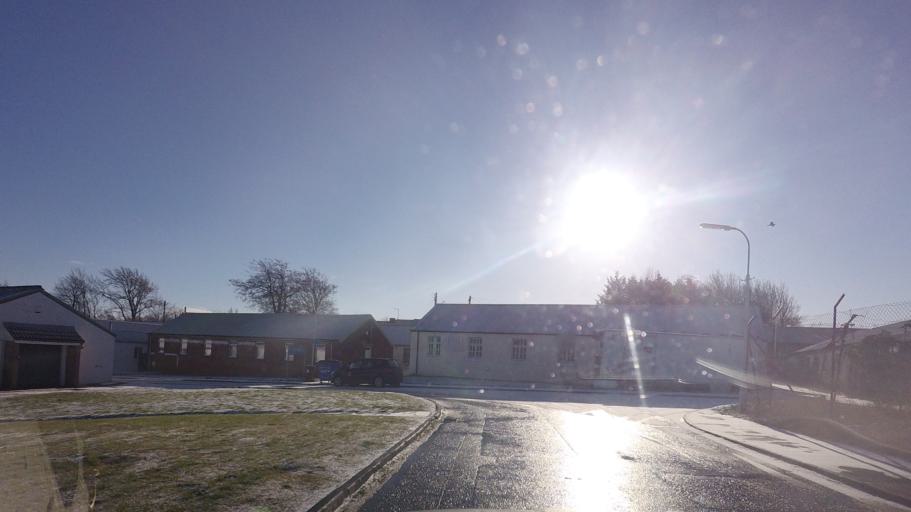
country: GB
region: Scotland
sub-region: Fife
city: Crossgates
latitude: 56.0454
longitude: -3.3452
